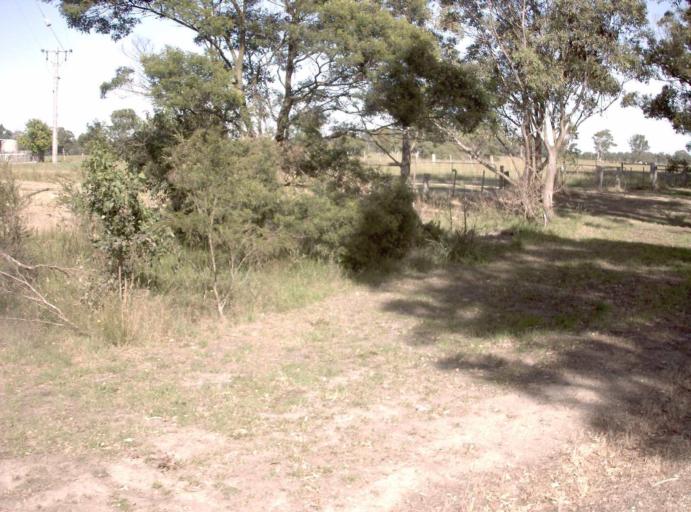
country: AU
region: Victoria
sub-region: East Gippsland
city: Lakes Entrance
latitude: -37.8105
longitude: 147.8450
